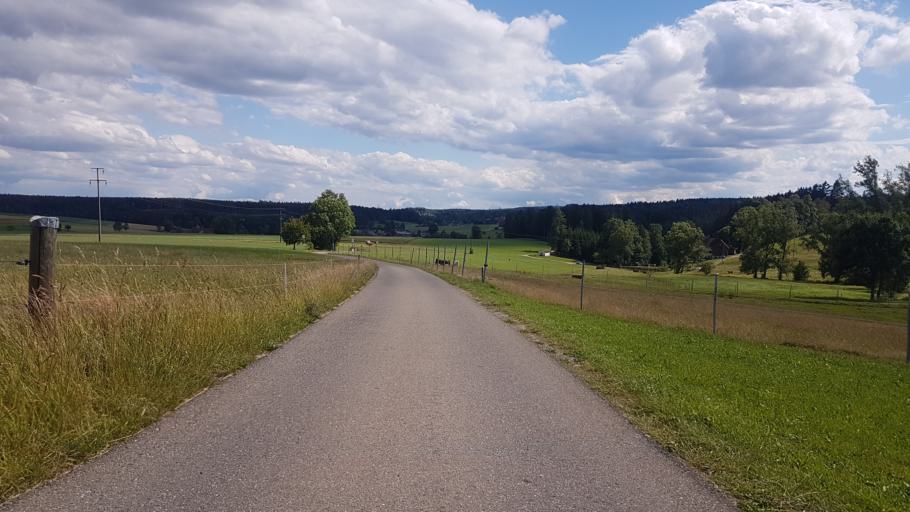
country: DE
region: Baden-Wuerttemberg
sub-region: Freiburg Region
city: Hardt
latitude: 48.1697
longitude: 8.4065
